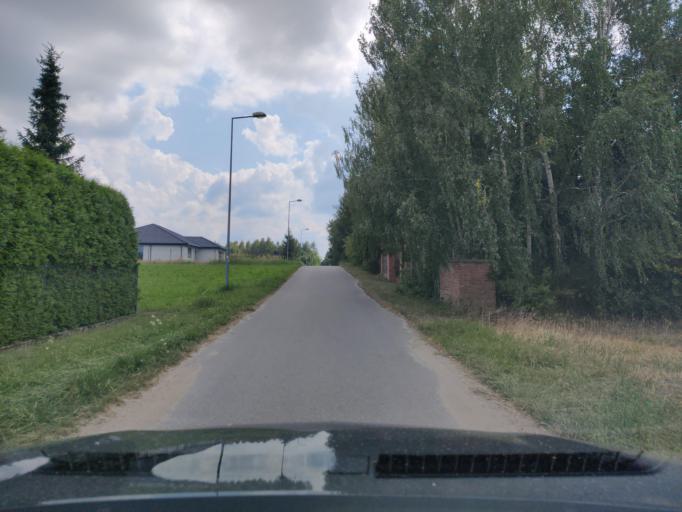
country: PL
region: Masovian Voivodeship
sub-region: Powiat pultuski
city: Zatory
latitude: 52.6110
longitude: 21.1125
